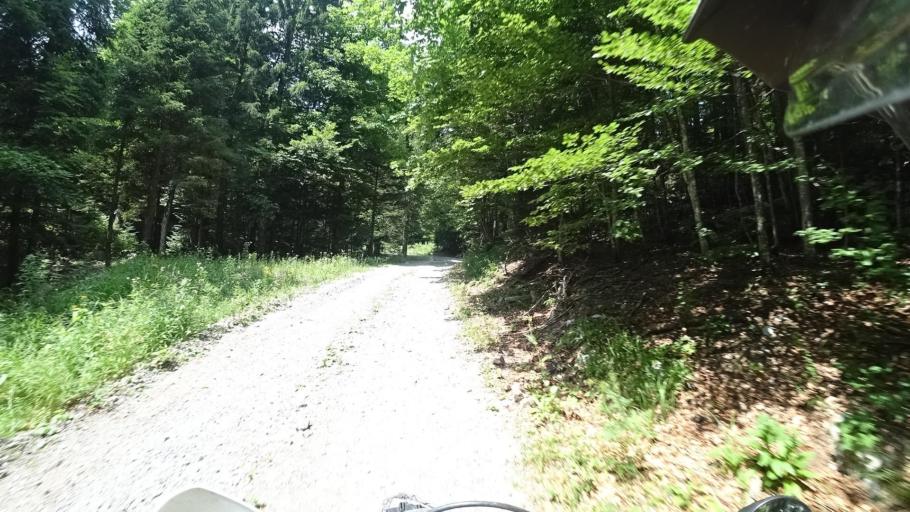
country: HR
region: Primorsko-Goranska
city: Vrbovsko
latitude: 45.3146
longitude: 15.0609
